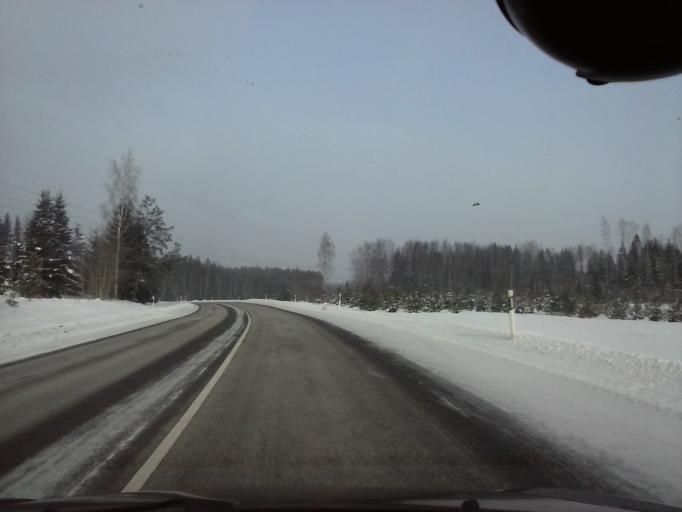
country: EE
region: Paernumaa
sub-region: Saarde vald
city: Kilingi-Nomme
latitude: 58.1952
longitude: 25.0625
